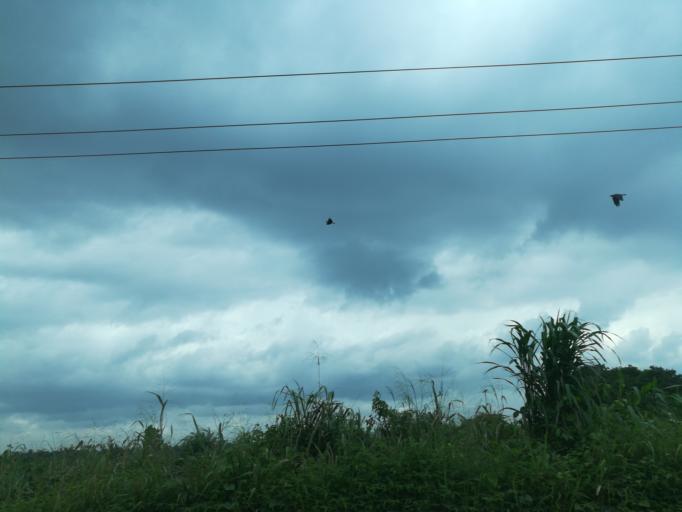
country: NG
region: Lagos
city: Ejirin
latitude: 6.6465
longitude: 3.8397
